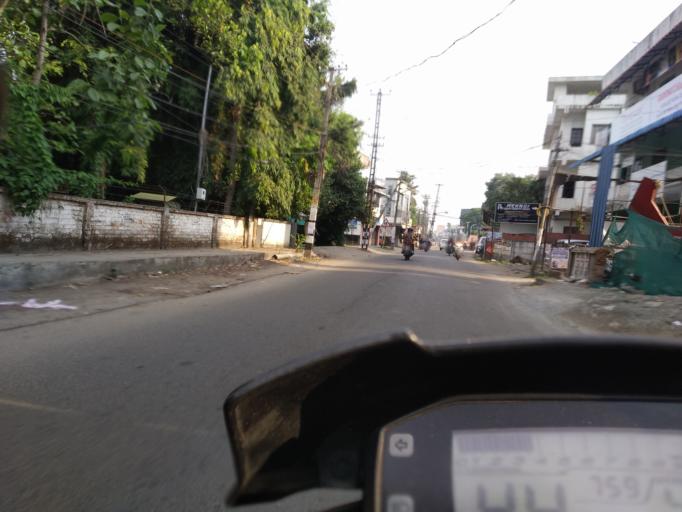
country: IN
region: Kerala
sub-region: Ernakulam
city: Cochin
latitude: 9.9717
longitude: 76.3171
